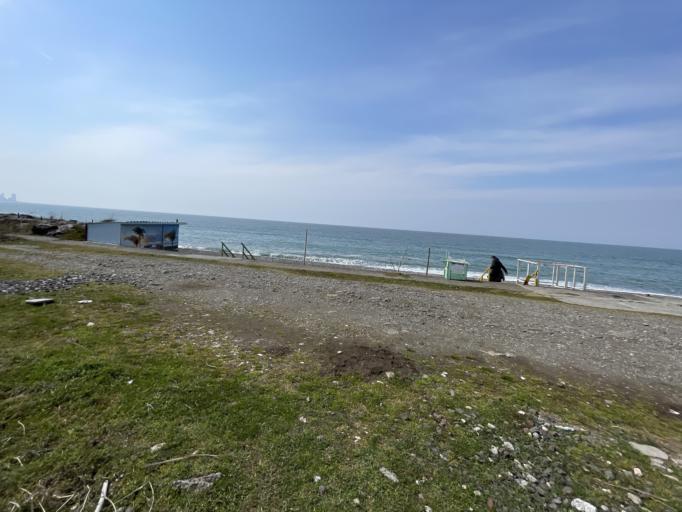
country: GE
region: Ajaria
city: Makhinjauri
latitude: 41.7058
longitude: 41.7187
